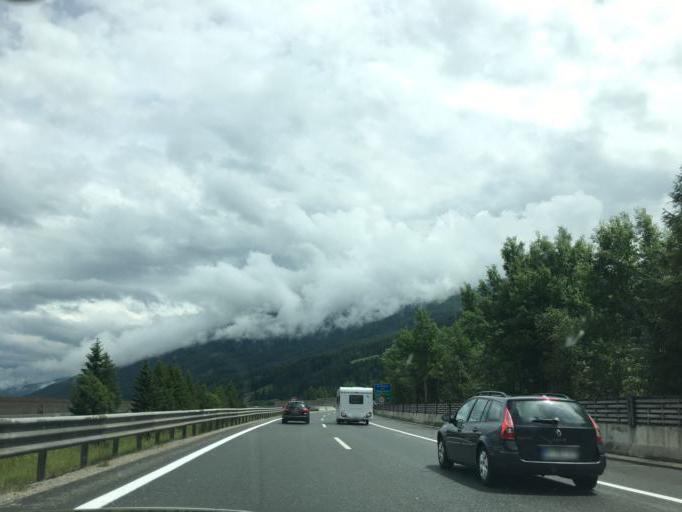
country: AT
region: Salzburg
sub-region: Politischer Bezirk Tamsweg
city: Sankt Michael im Lungau
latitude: 47.0980
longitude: 13.6054
